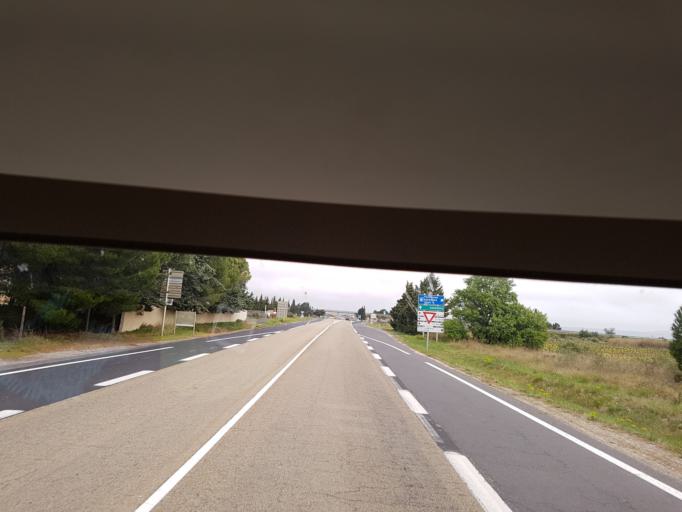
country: FR
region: Languedoc-Roussillon
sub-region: Departement de l'Aude
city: Leucate
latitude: 42.9328
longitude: 2.9923
